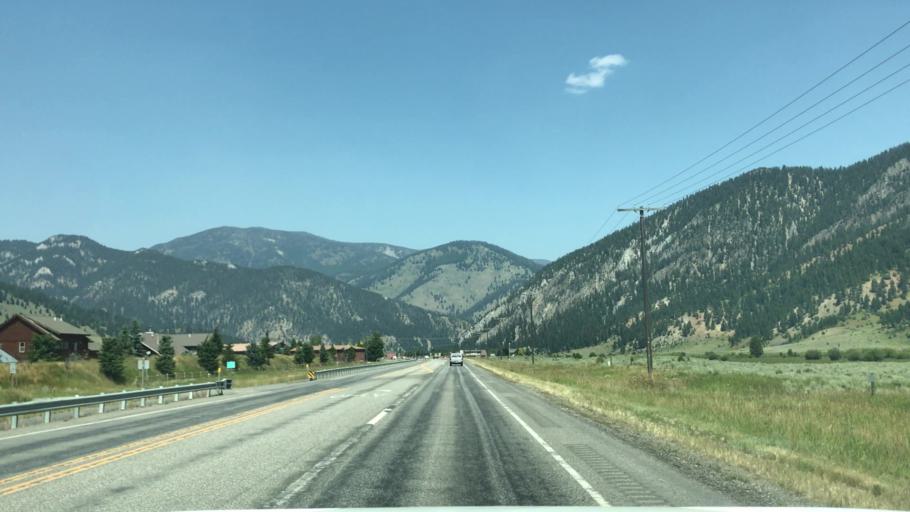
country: US
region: Montana
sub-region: Gallatin County
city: Big Sky
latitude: 45.2416
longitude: -111.2508
